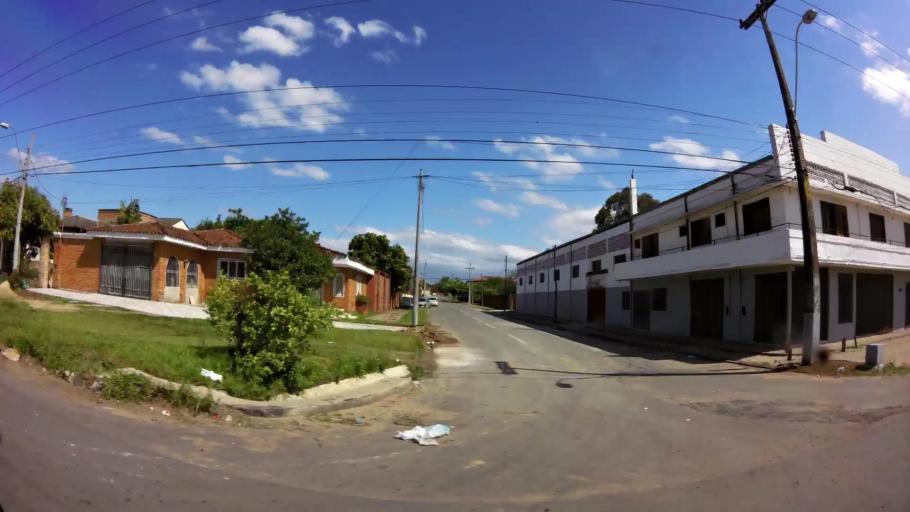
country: PY
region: Central
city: Fernando de la Mora
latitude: -25.2810
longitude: -57.5364
